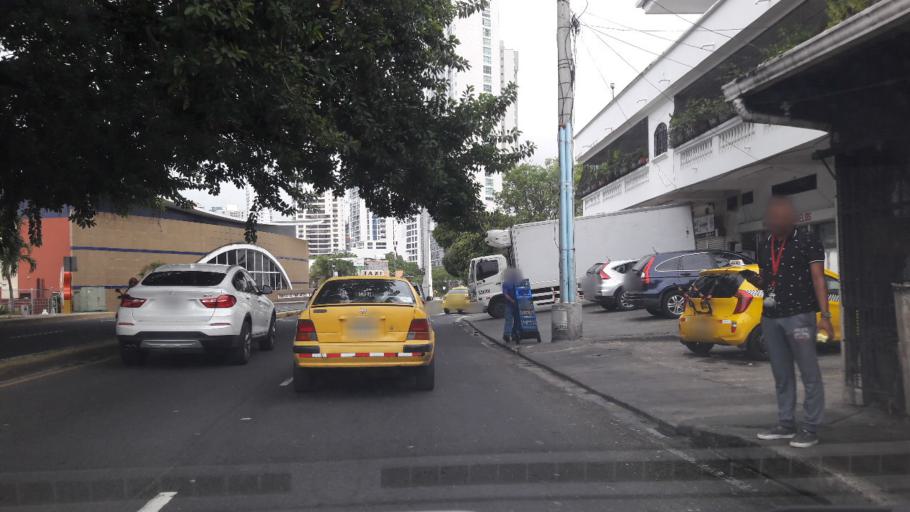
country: PA
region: Panama
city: Panama
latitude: 9.0046
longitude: -79.4932
